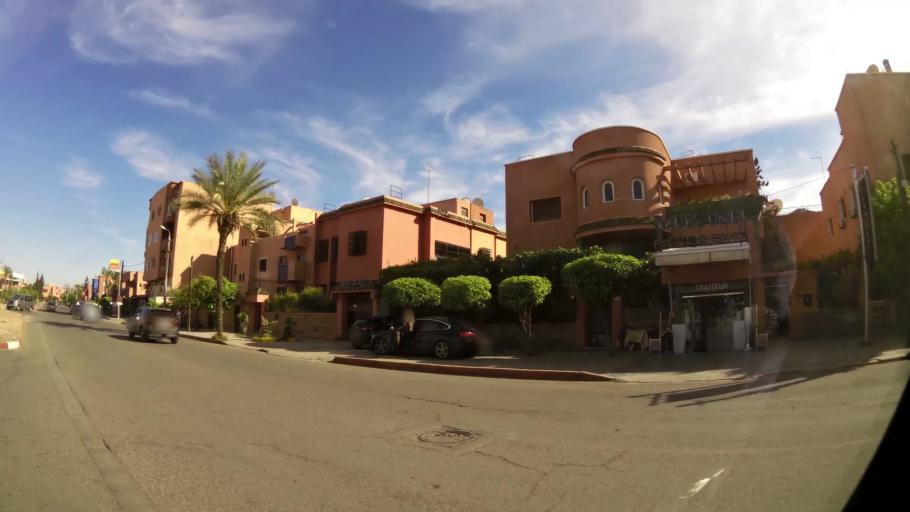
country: MA
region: Marrakech-Tensift-Al Haouz
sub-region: Marrakech
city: Marrakesh
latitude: 31.6562
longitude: -8.0125
